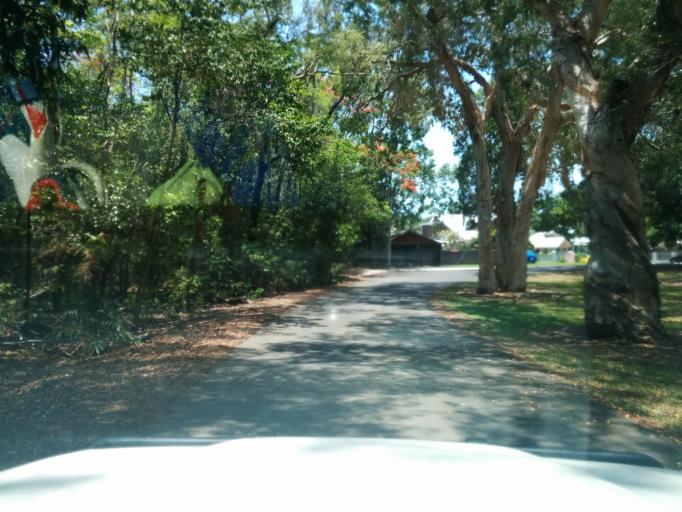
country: AU
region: Queensland
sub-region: Cairns
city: Yorkeys Knob
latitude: -16.8302
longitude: 145.7335
